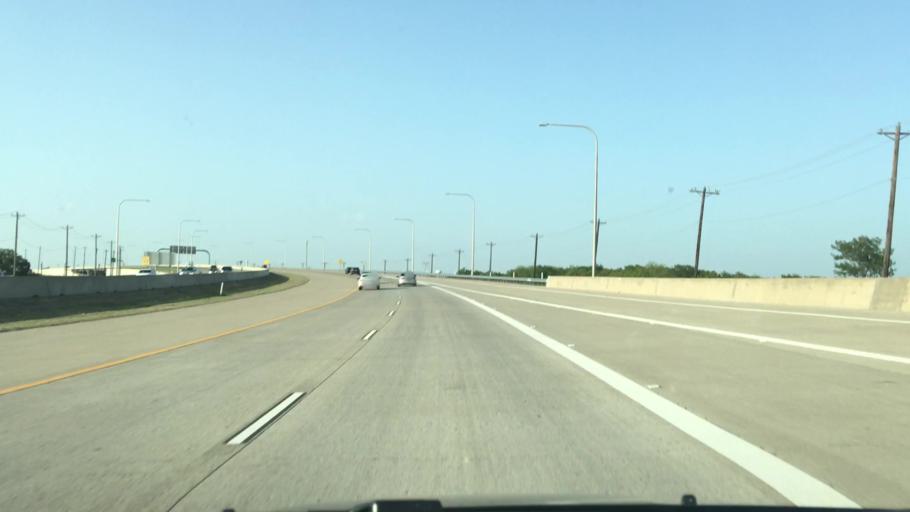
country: US
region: Texas
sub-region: Collin County
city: Prosper
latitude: 33.2038
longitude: -96.8224
